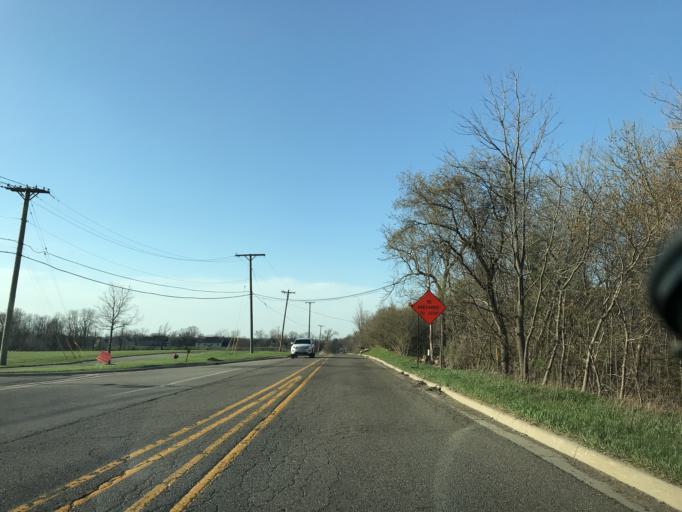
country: US
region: Michigan
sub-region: Oakland County
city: Wixom
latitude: 42.4662
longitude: -83.5636
